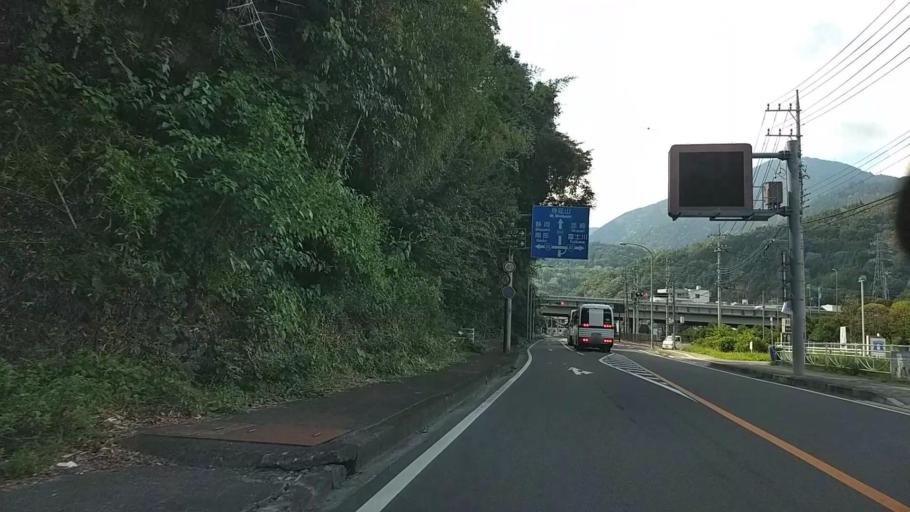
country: JP
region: Shizuoka
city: Fujinomiya
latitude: 35.3690
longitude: 138.4462
